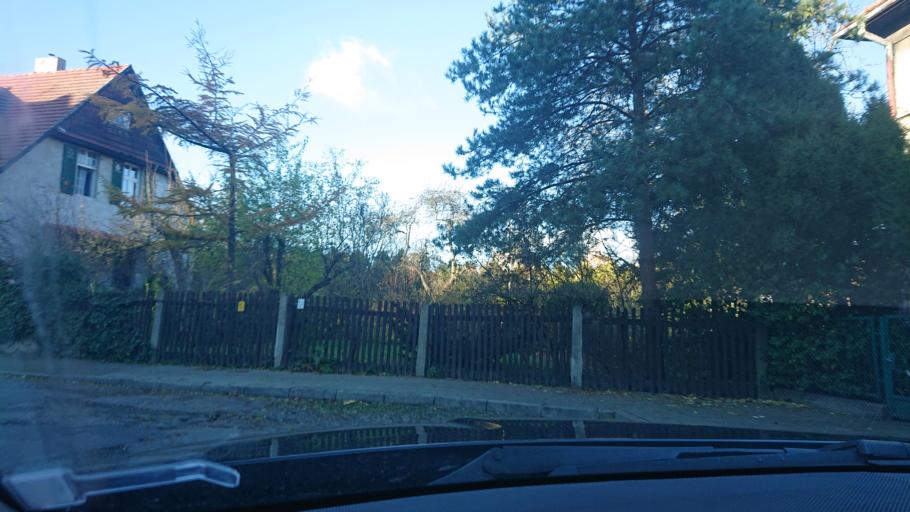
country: PL
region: Greater Poland Voivodeship
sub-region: Powiat gnieznienski
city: Gniezno
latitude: 52.5385
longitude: 17.6062
